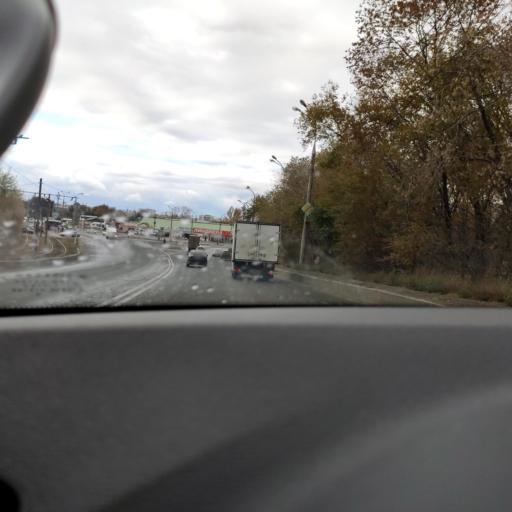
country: RU
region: Samara
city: Smyshlyayevka
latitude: 53.2226
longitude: 50.2891
